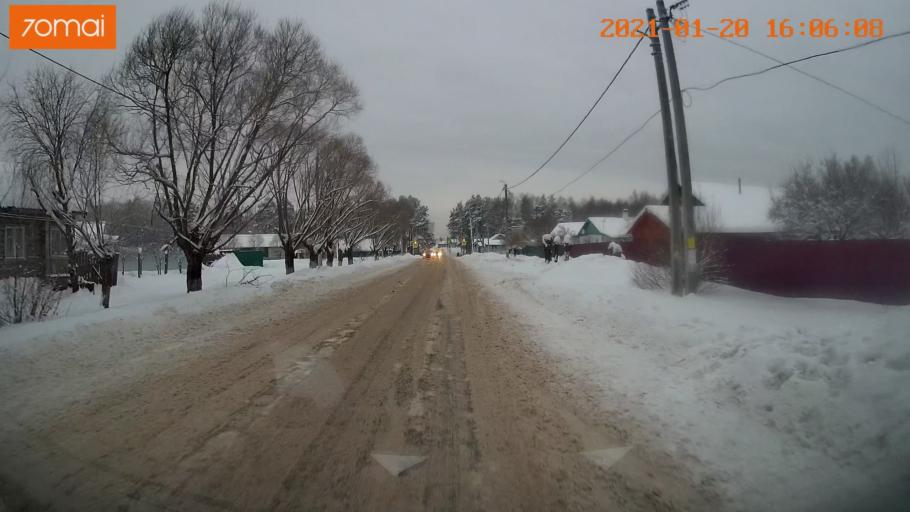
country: RU
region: Vladimir
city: Sudogda
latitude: 56.0693
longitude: 40.7966
